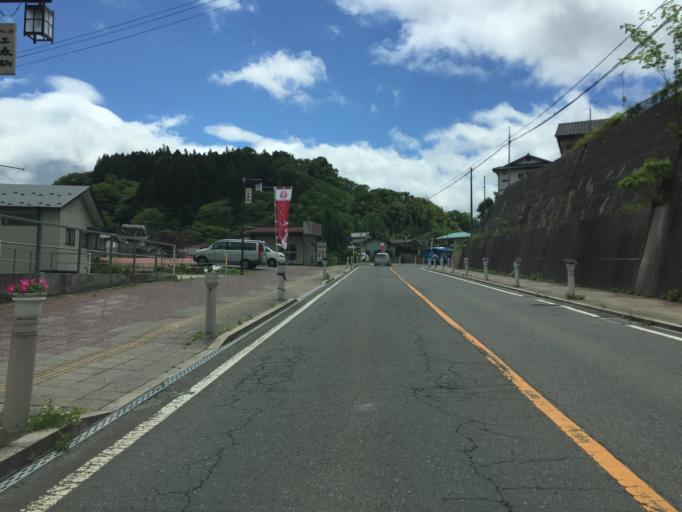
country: JP
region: Fukushima
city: Miharu
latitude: 37.4466
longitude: 140.4875
